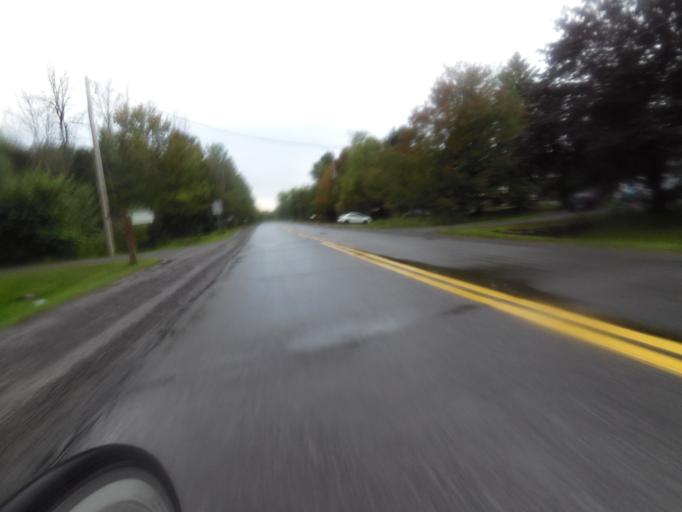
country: CA
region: Ontario
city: Bells Corners
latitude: 45.1957
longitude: -75.7186
